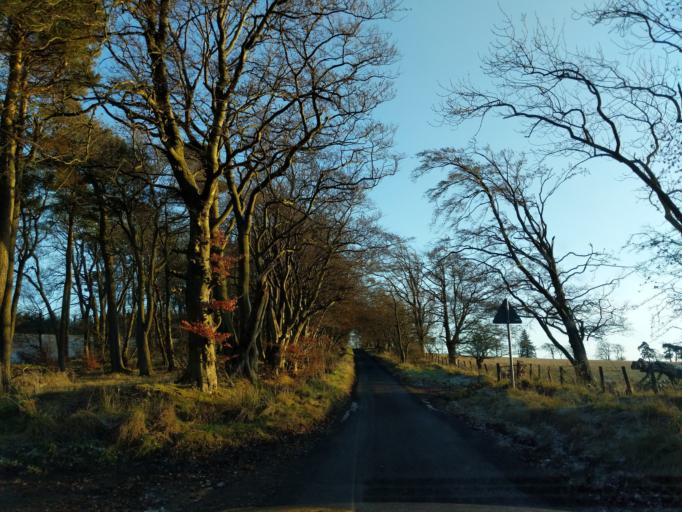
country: GB
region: Scotland
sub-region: Edinburgh
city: Balerno
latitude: 55.8603
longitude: -3.3667
